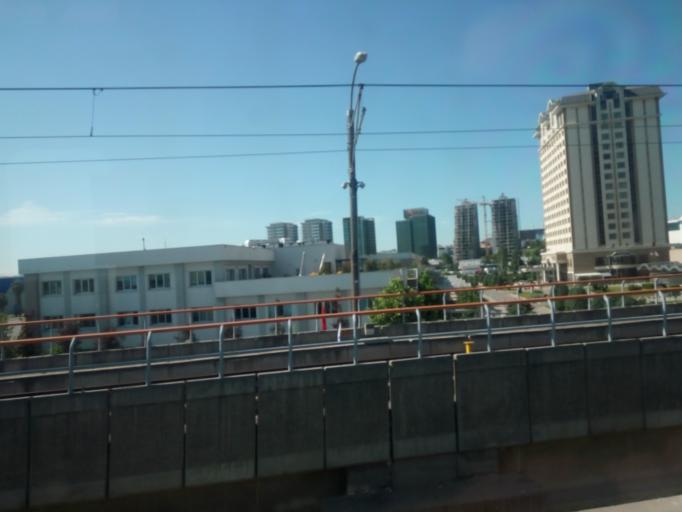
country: TR
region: Istanbul
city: Bahcelievler
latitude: 40.9870
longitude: 28.8297
